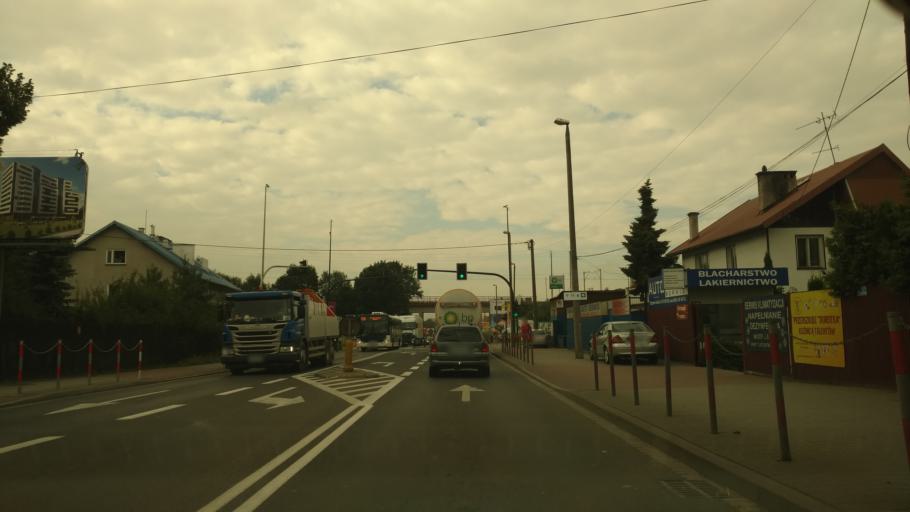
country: PL
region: Lesser Poland Voivodeship
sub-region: Krakow
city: Krakow
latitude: 50.0979
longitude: 19.9622
